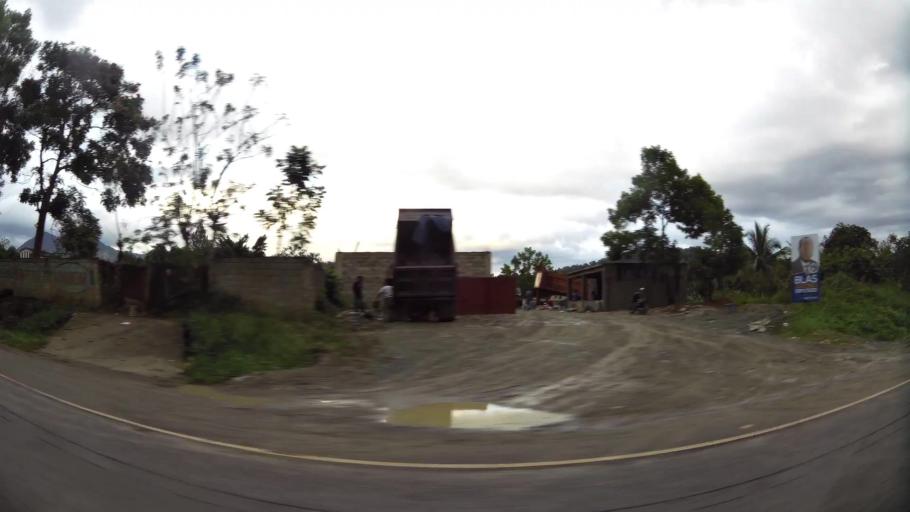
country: DO
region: San Cristobal
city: Villa Altagracia
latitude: 18.6355
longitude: -70.1679
